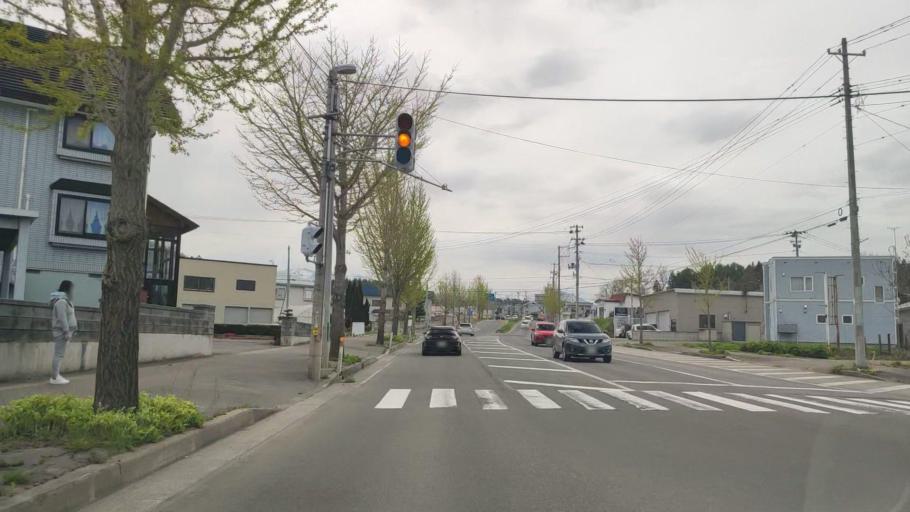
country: JP
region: Aomori
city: Aomori Shi
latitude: 40.7921
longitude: 140.7864
